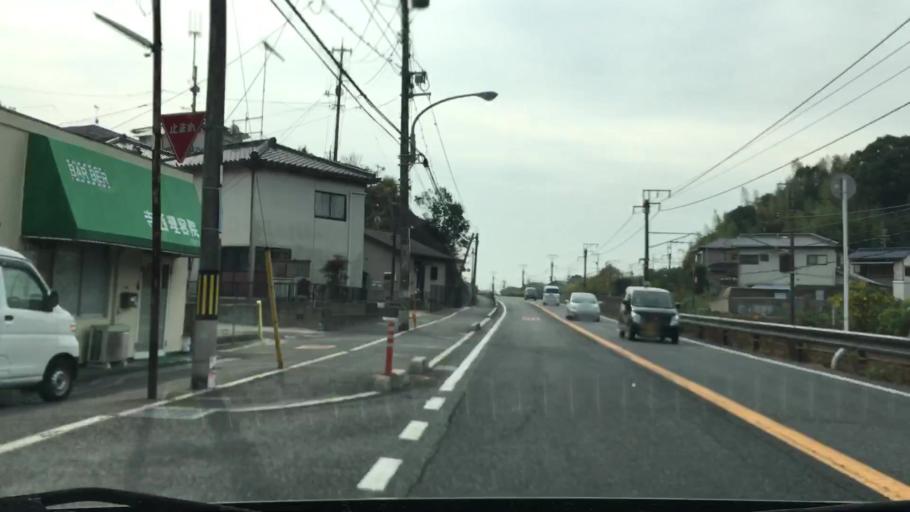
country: JP
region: Hiroshima
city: Ono-hara
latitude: 34.2785
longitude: 132.2624
